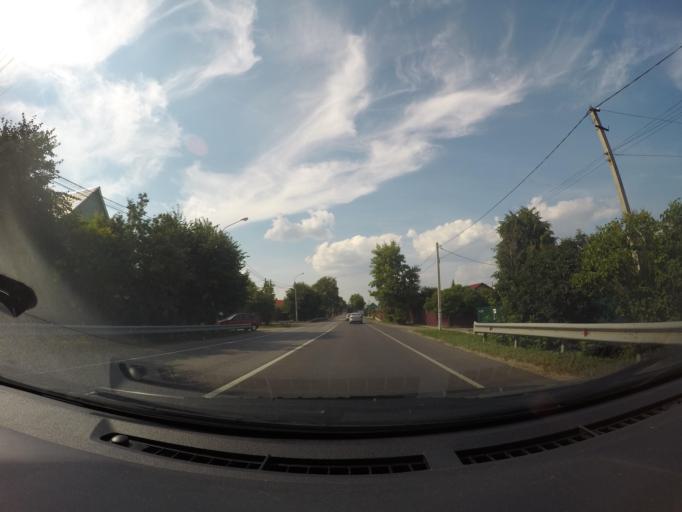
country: RU
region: Moskovskaya
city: Gzhel'
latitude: 55.6101
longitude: 38.3953
